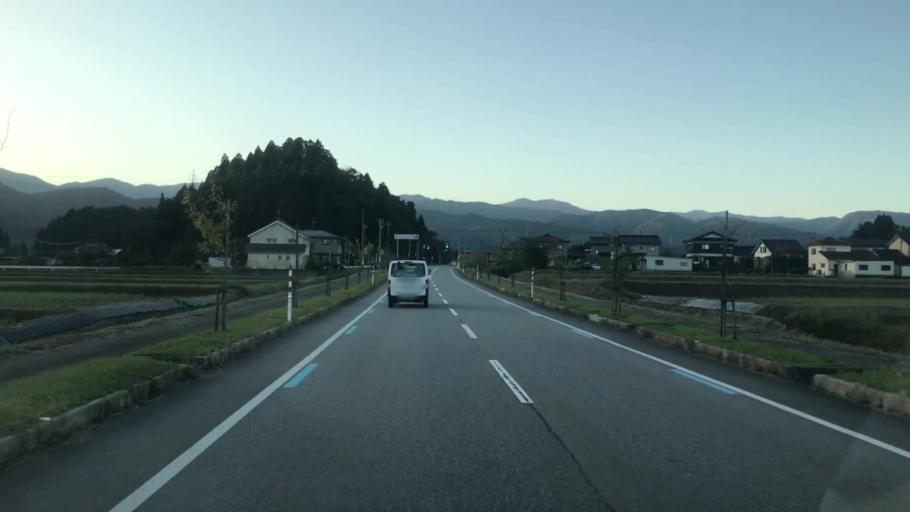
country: JP
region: Toyama
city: Kamiichi
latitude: 36.6087
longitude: 137.3250
